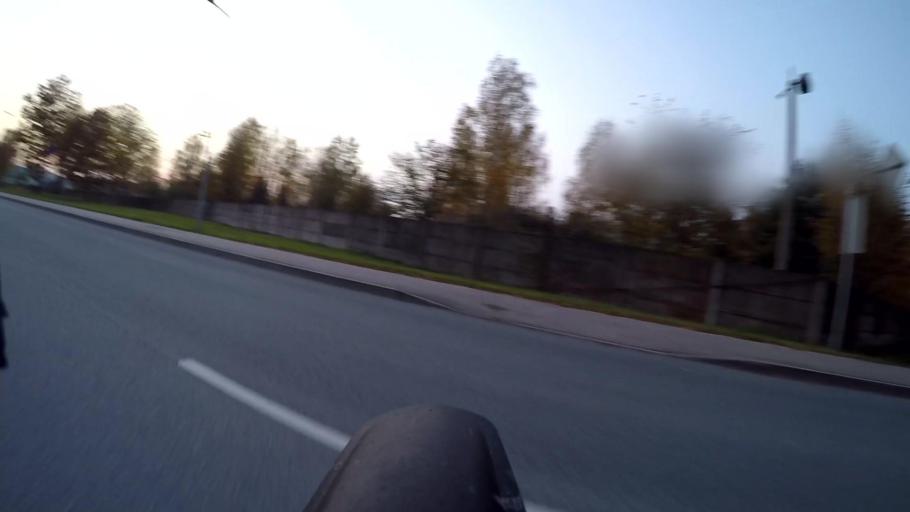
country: LV
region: Marupe
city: Marupe
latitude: 56.9187
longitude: 23.9887
